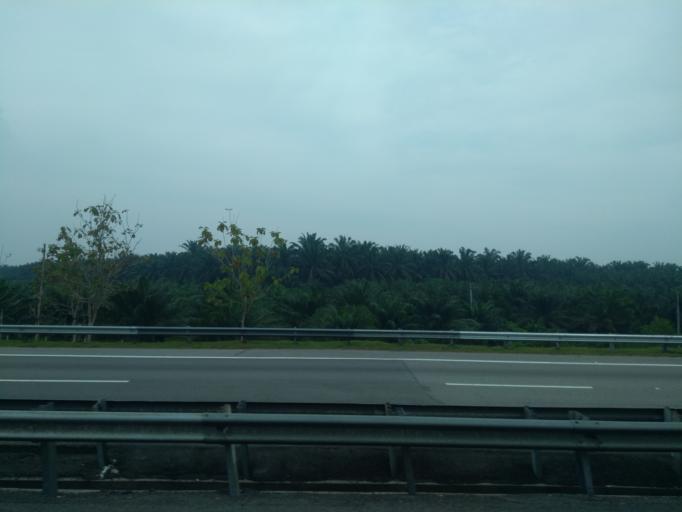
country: MY
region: Perak
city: Taiping
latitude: 4.7925
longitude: 100.6925
